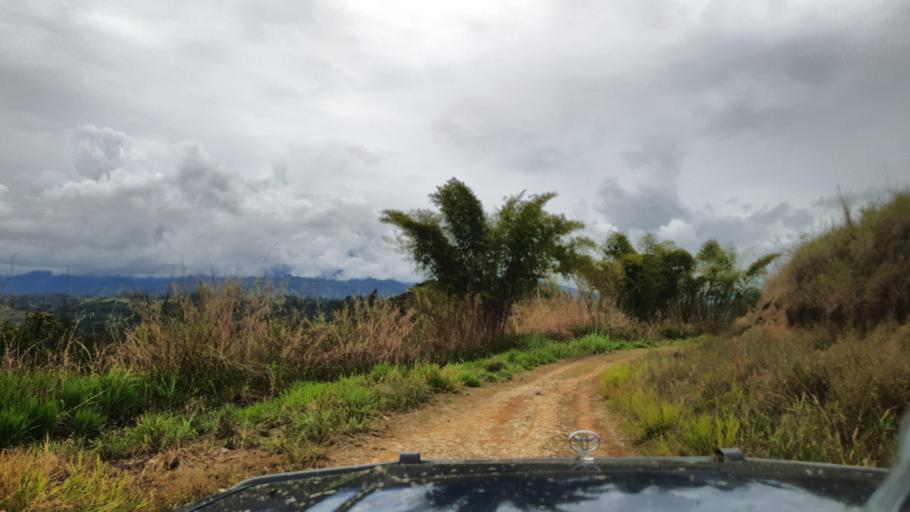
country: PG
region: Jiwaka
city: Minj
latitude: -5.9278
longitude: 144.7463
